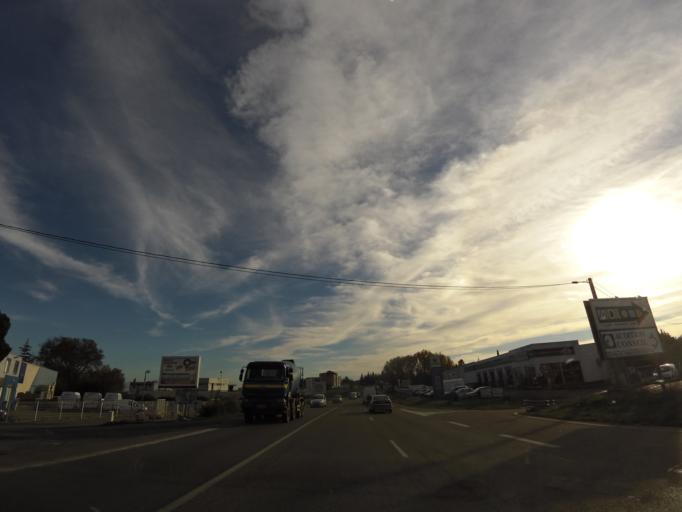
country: FR
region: Languedoc-Roussillon
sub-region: Departement du Gard
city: Ales
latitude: 44.1204
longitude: 4.1090
